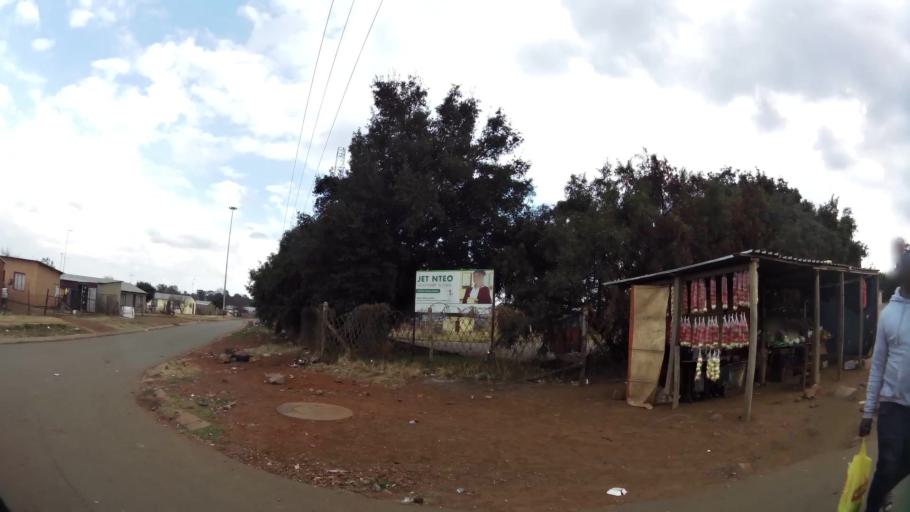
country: ZA
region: Gauteng
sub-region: Sedibeng District Municipality
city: Vanderbijlpark
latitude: -26.6634
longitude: 27.8469
